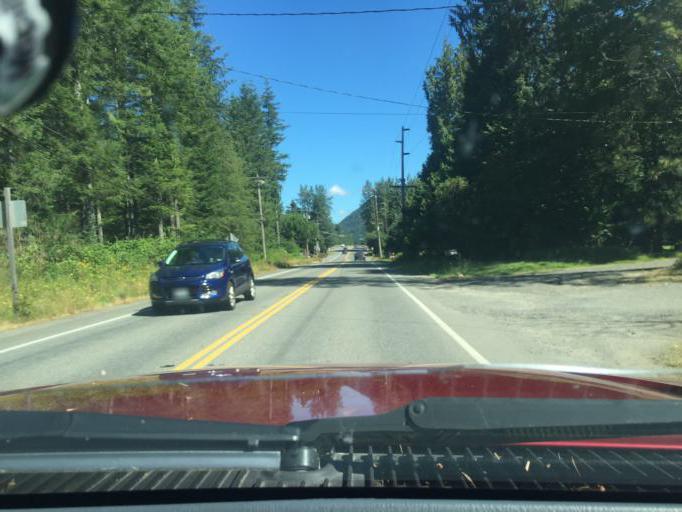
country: US
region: Washington
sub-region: King County
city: Riverbend
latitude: 47.4692
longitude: -121.7584
